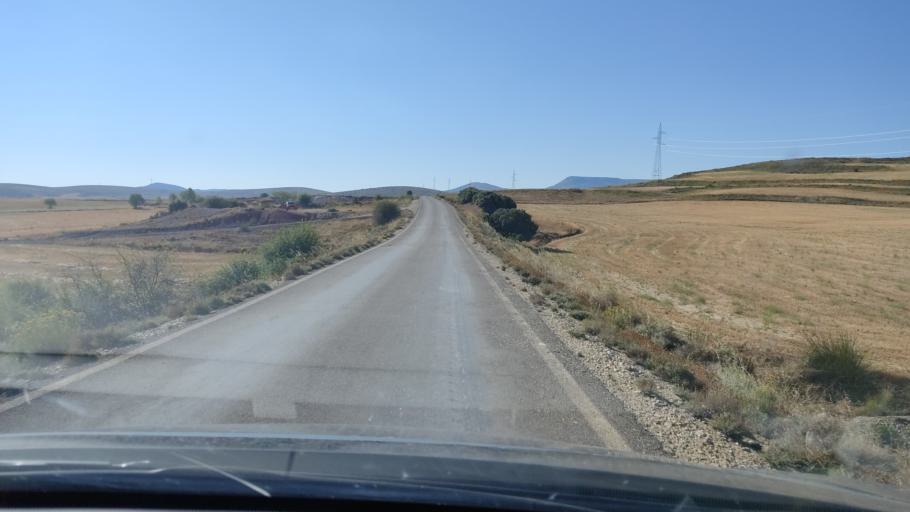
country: ES
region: Aragon
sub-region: Provincia de Teruel
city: Monforte de Moyuela
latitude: 41.0392
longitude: -0.9821
